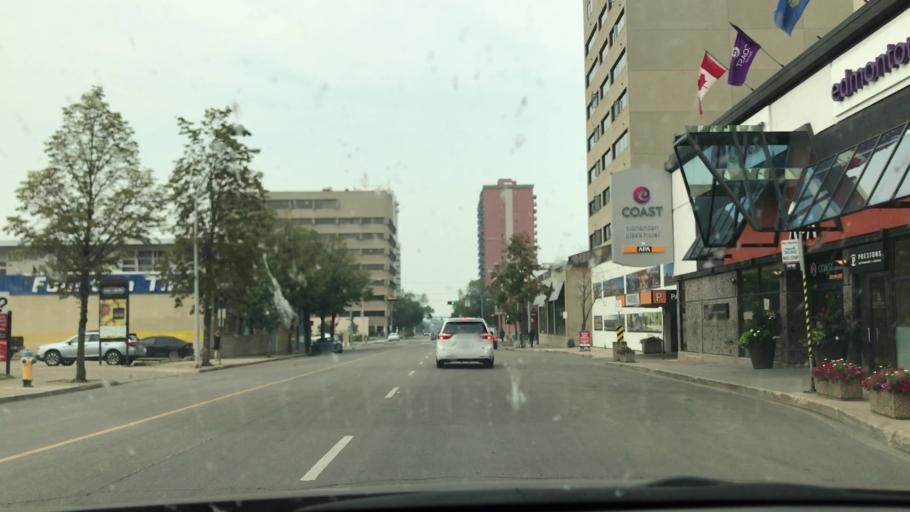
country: CA
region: Alberta
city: Edmonton
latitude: 53.5419
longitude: -113.5011
